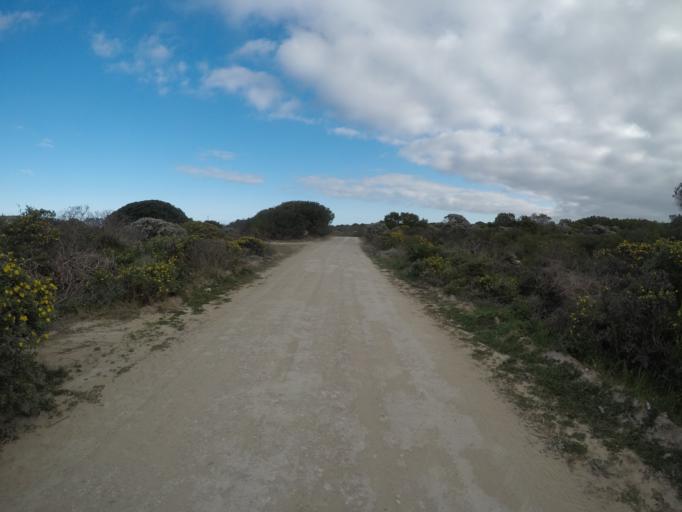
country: ZA
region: Western Cape
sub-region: Eden District Municipality
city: Riversdale
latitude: -34.4230
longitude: 21.3306
